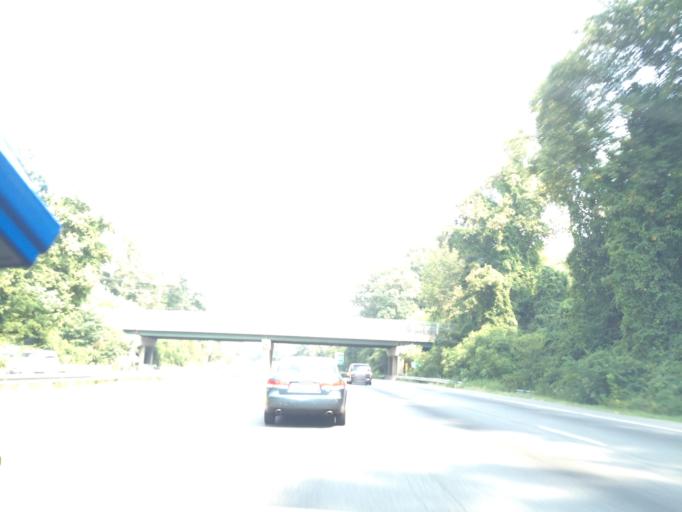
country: US
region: Maryland
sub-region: Montgomery County
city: North Bethesda
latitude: 39.0130
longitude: -77.1347
